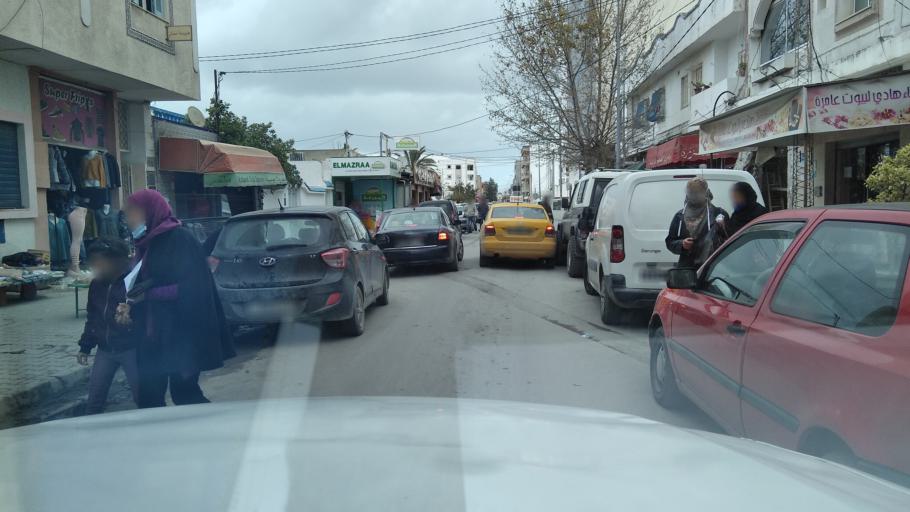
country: TN
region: Bin 'Arus
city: Ben Arous
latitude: 36.7559
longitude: 10.2215
